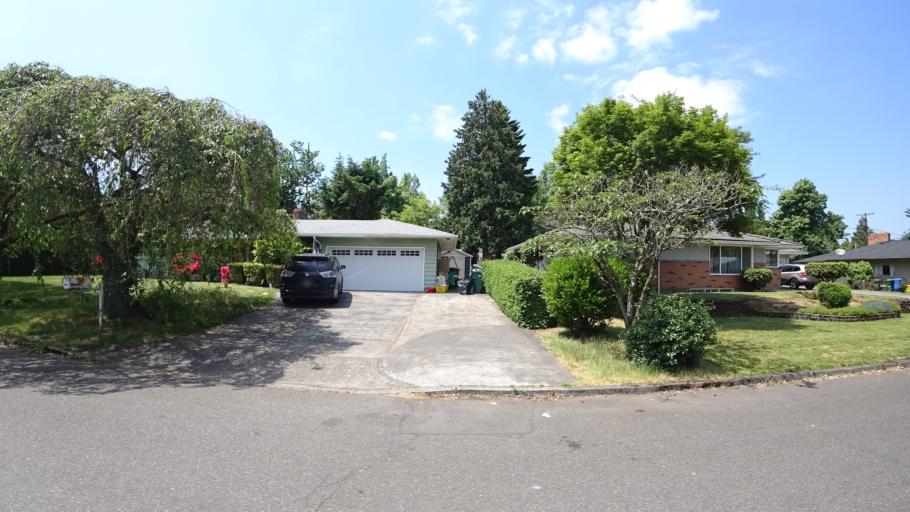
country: US
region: Oregon
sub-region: Multnomah County
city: Fairview
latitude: 45.5339
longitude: -122.5050
